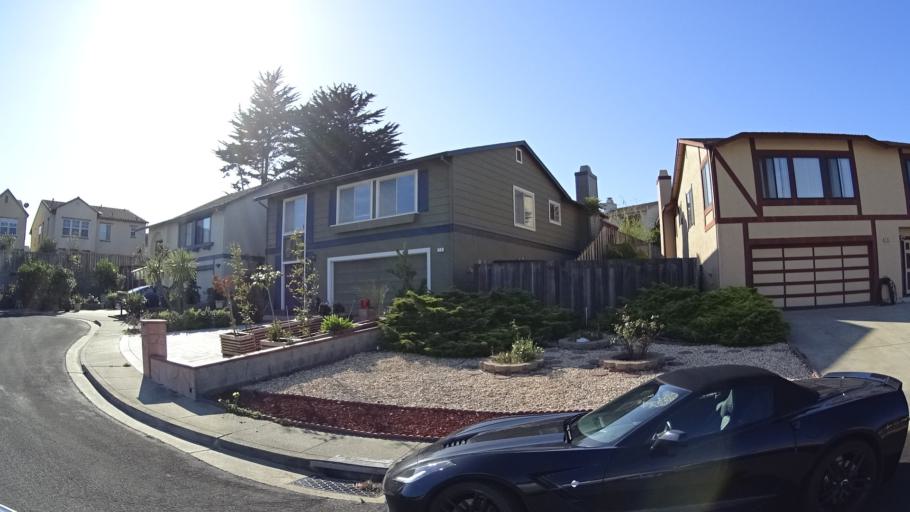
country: US
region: California
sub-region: San Mateo County
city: San Bruno
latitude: 37.6372
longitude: -122.4463
